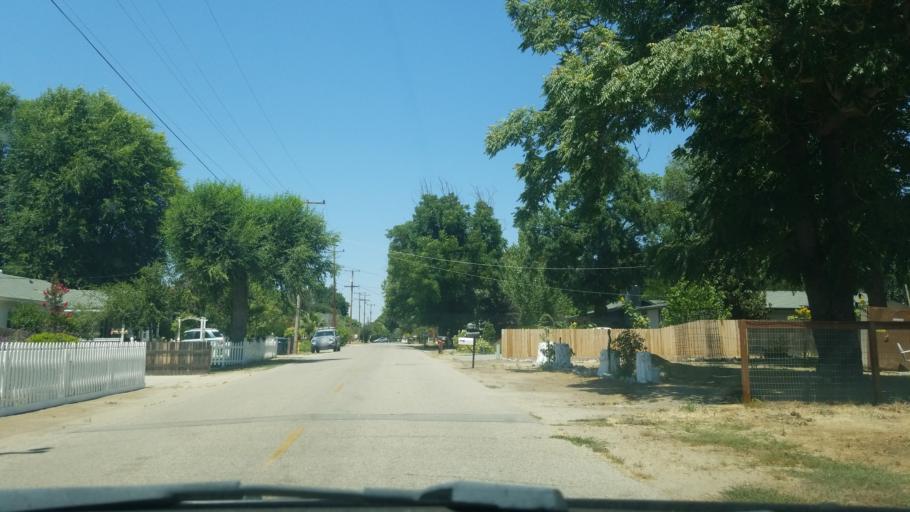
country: US
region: California
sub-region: San Luis Obispo County
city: Atascadero
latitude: 35.5061
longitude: -120.6634
